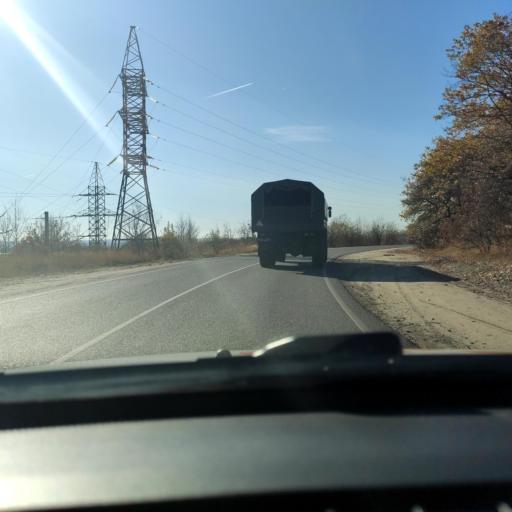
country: RU
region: Voronezj
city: Shilovo
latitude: 51.5617
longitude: 39.1401
